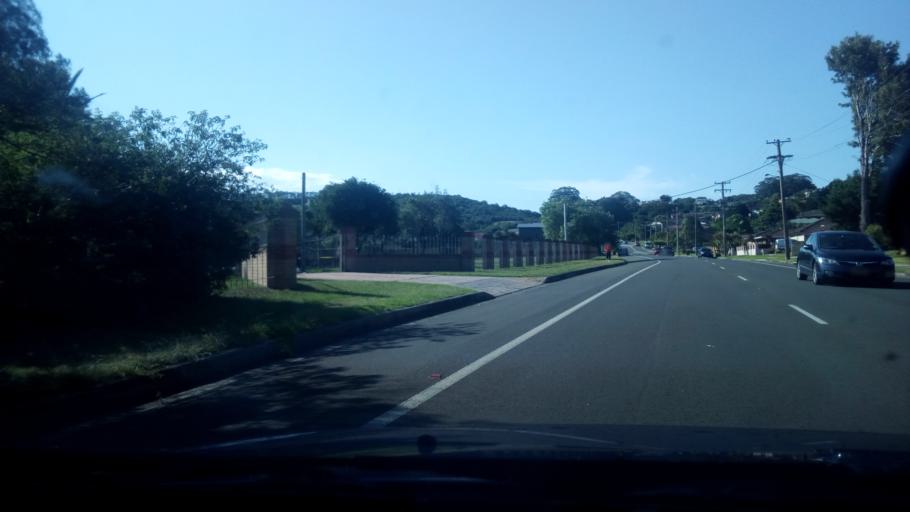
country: AU
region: New South Wales
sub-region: Wollongong
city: Berkeley
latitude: -34.4764
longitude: 150.8550
